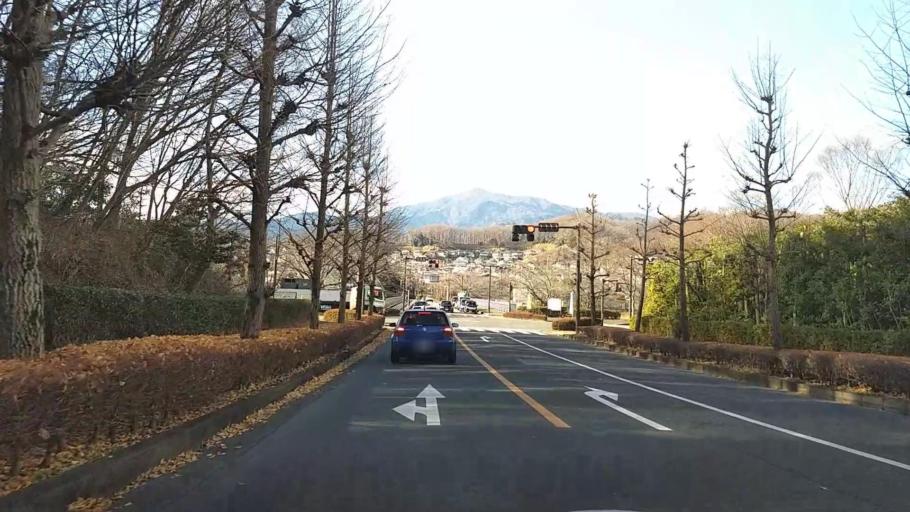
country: JP
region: Kanagawa
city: Atsugi
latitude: 35.4418
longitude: 139.3128
